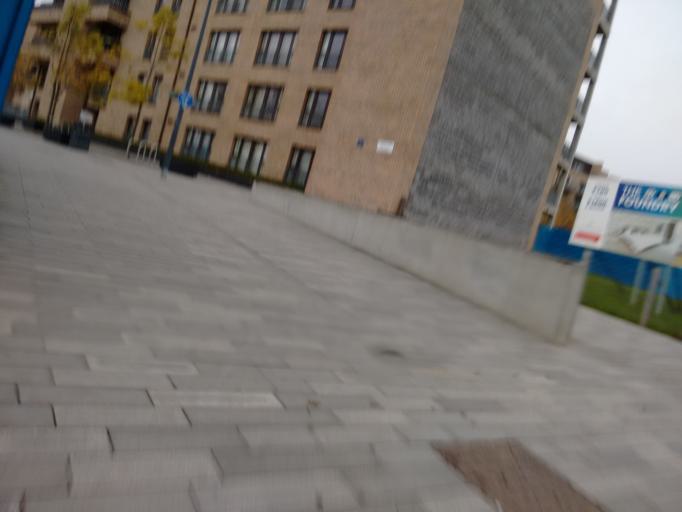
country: GB
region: Scotland
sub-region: Edinburgh
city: Edinburgh
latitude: 55.9425
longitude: -3.2129
